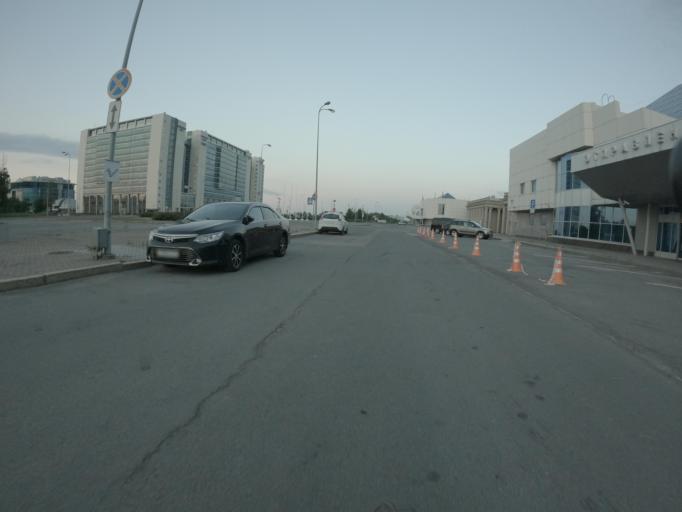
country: RU
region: St.-Petersburg
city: Dachnoye
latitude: 59.8067
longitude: 30.3077
